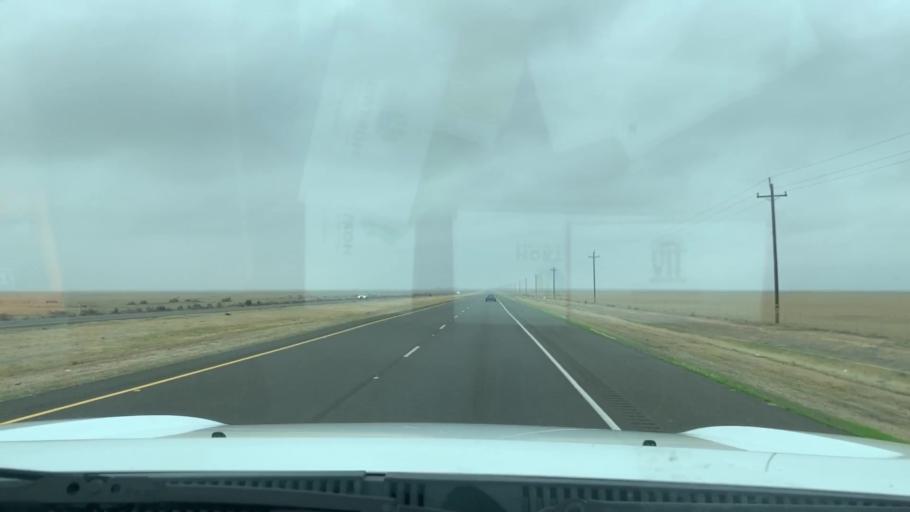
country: US
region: California
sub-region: Kern County
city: Lost Hills
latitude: 35.6158
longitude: -119.7904
